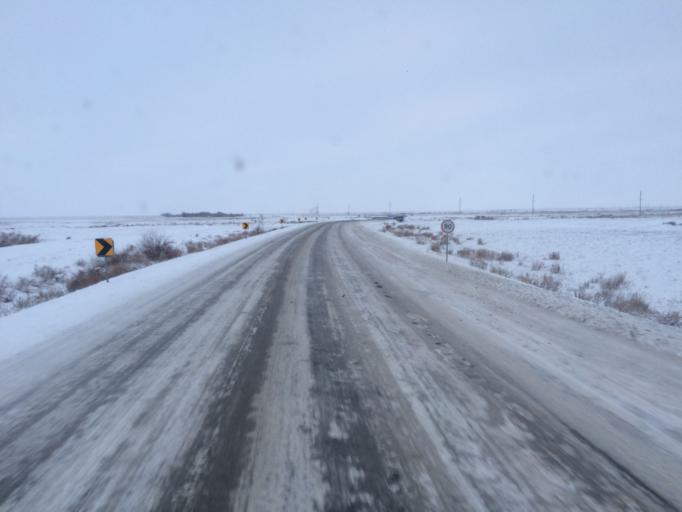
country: KZ
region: Batys Qazaqstan
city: Dzhambeyty
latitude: 50.6280
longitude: 52.1172
